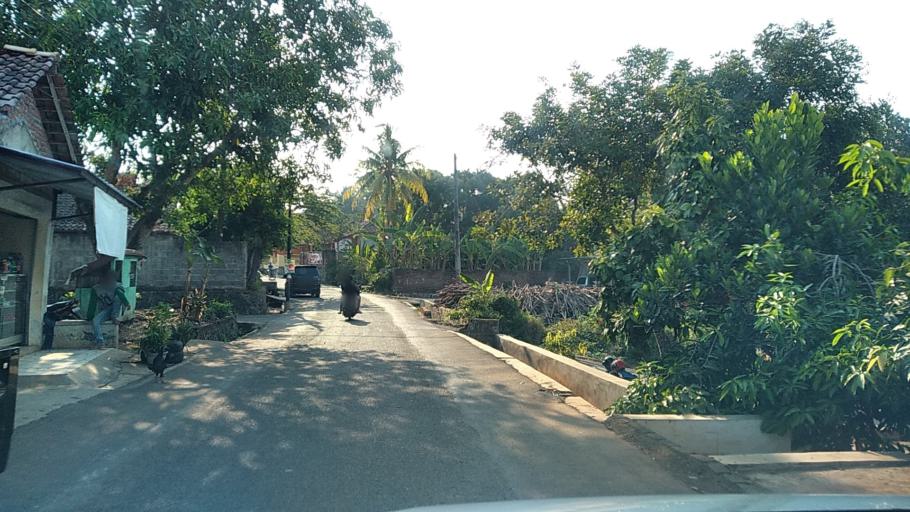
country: ID
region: Central Java
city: Semarang
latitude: -7.0386
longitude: 110.2926
